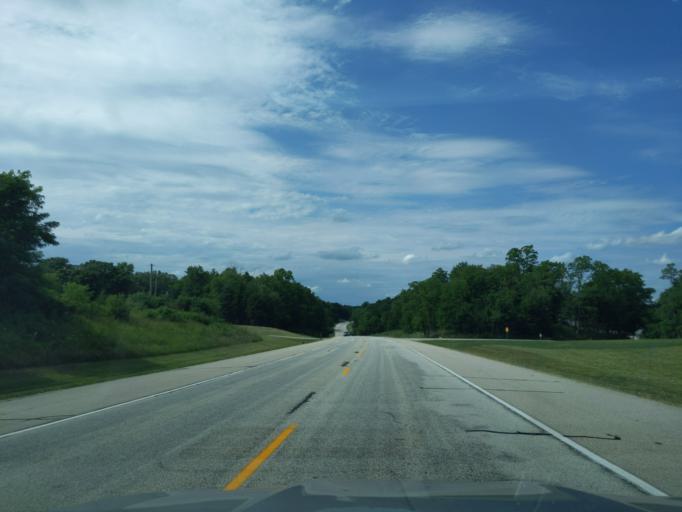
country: US
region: Indiana
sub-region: Ripley County
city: Batesville
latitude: 39.2053
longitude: -85.2078
